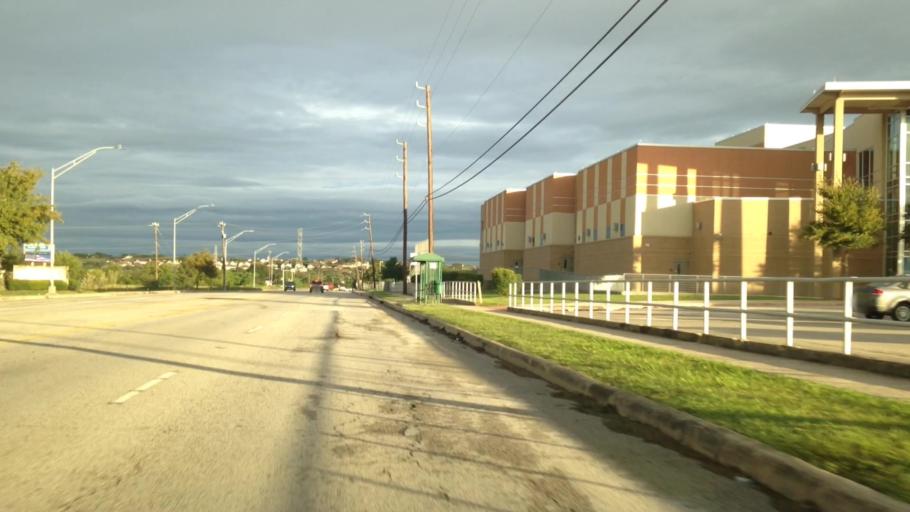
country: US
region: Texas
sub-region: Bexar County
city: Live Oak
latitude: 29.5811
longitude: -98.3928
